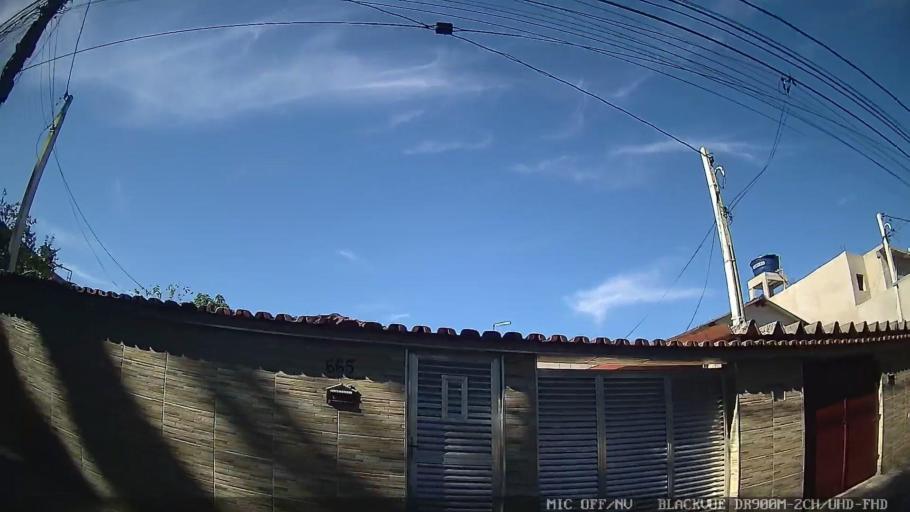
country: BR
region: Sao Paulo
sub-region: Santos
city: Santos
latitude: -23.9377
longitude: -46.2860
